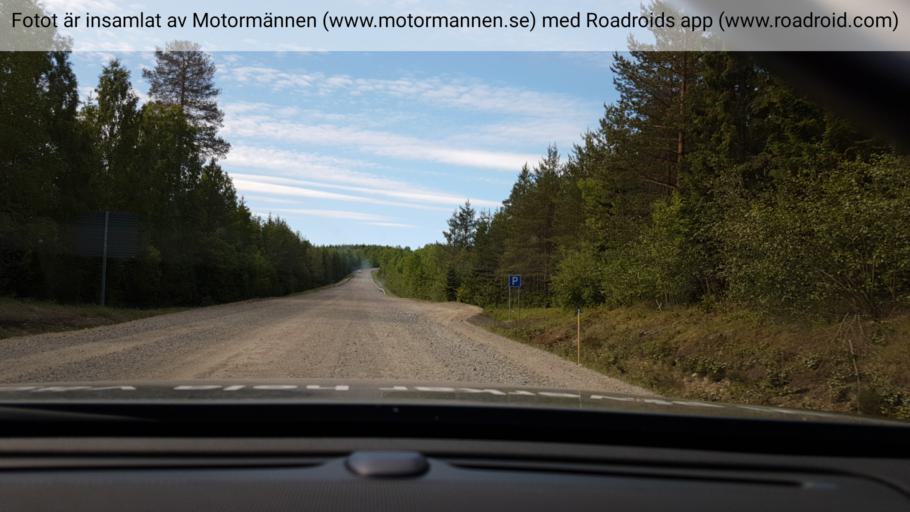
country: SE
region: Vaesterbotten
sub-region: Bjurholms Kommun
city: Bjurholm
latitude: 63.9256
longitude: 19.1871
